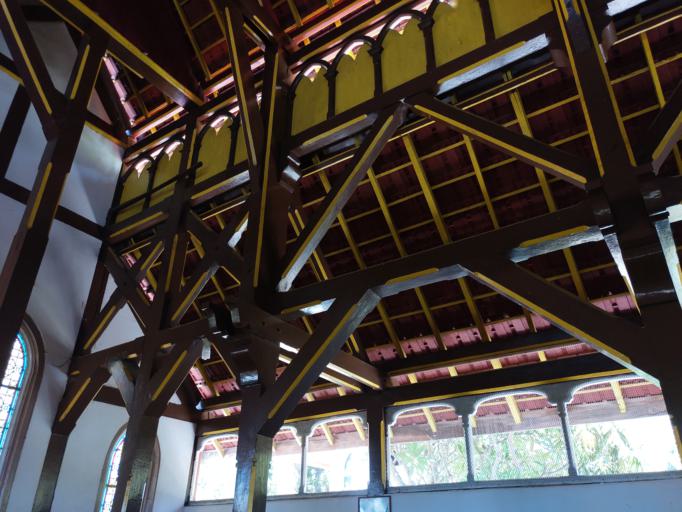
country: ID
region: East Nusa Tenggara
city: Sikka
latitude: -8.7495
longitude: 122.1968
